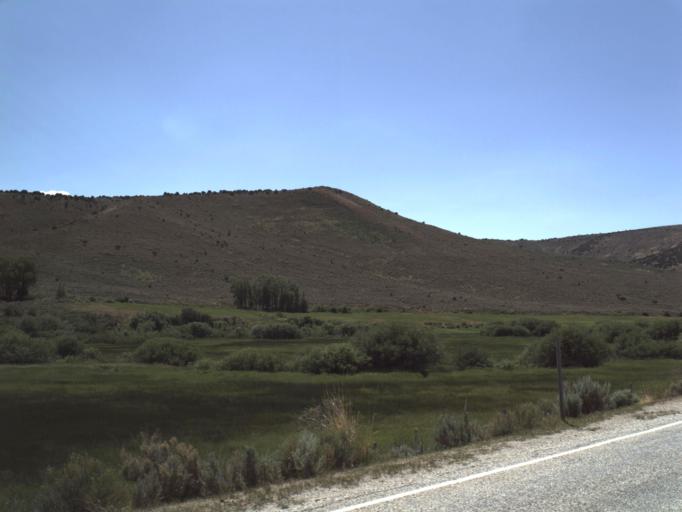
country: US
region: Utah
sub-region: Rich County
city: Randolph
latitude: 41.4953
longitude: -111.2604
